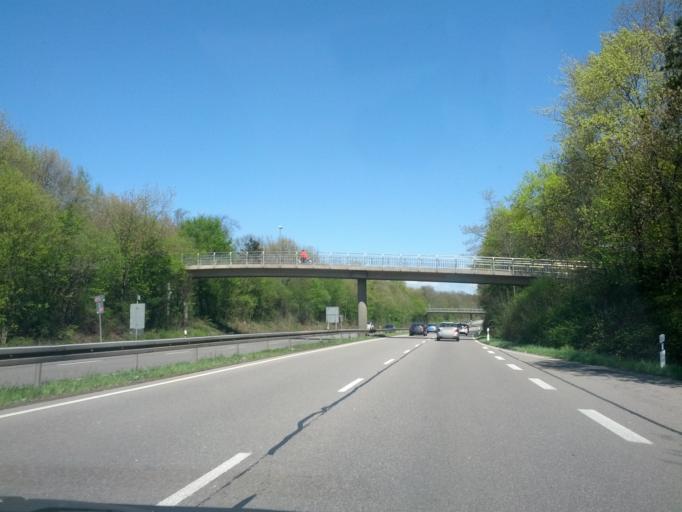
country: DE
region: Baden-Wuerttemberg
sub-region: Freiburg Region
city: Umkirch
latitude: 48.0157
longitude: 7.8099
